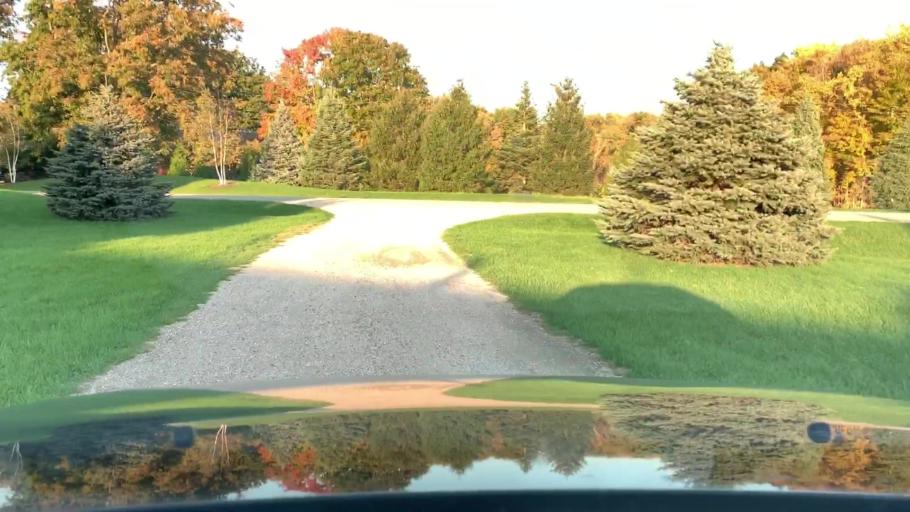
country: US
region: Michigan
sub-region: Ottawa County
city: Hudsonville
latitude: 42.7764
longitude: -85.8426
